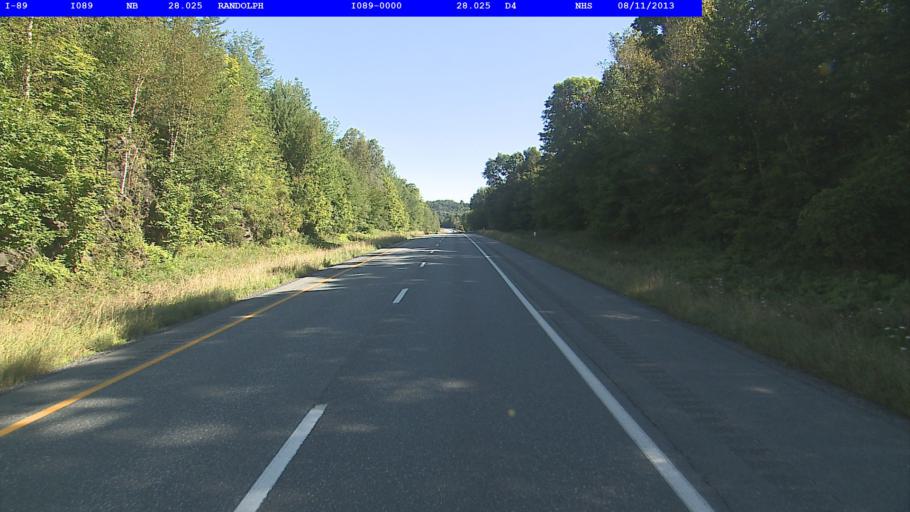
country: US
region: Vermont
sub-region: Orange County
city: Randolph
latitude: 43.9040
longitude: -72.6139
